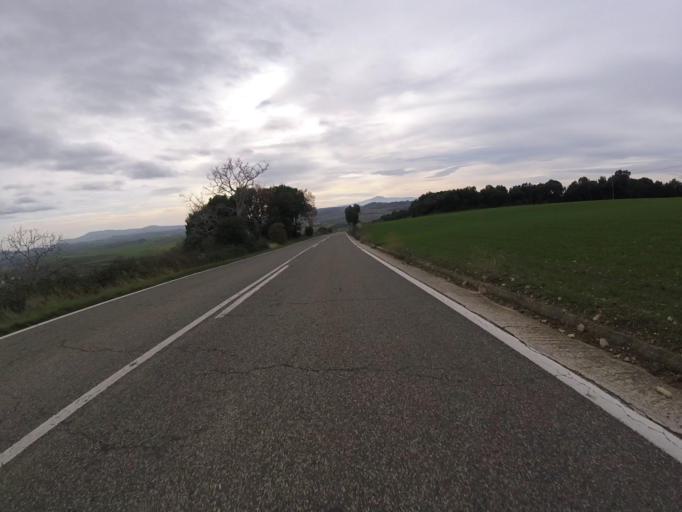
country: ES
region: Navarre
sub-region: Provincia de Navarra
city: Lezaun
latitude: 42.7317
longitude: -2.0156
